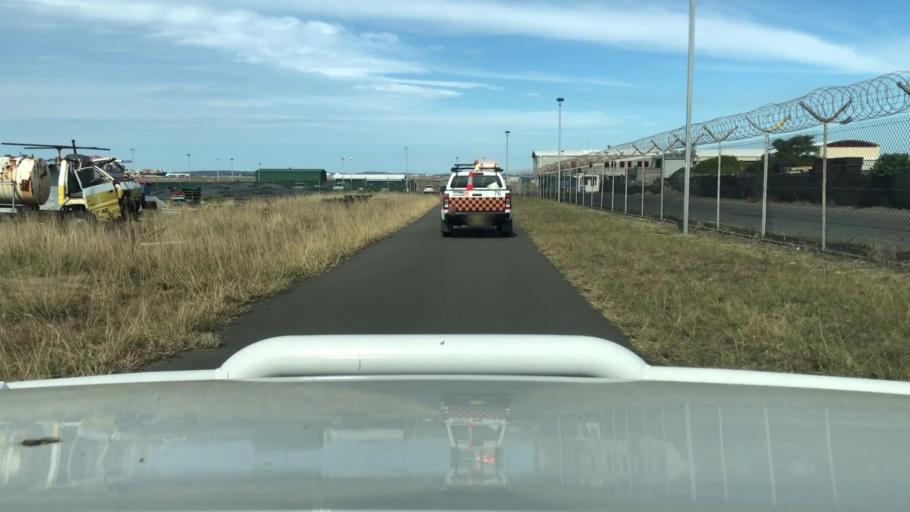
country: AU
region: New South Wales
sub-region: Botany Bay
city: Botany
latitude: -33.9473
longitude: 151.1854
